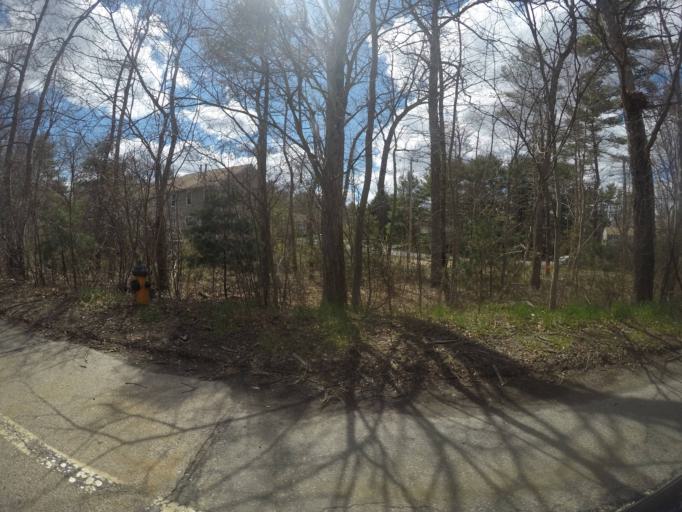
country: US
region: Massachusetts
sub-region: Bristol County
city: Easton
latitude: 42.0288
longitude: -71.0699
